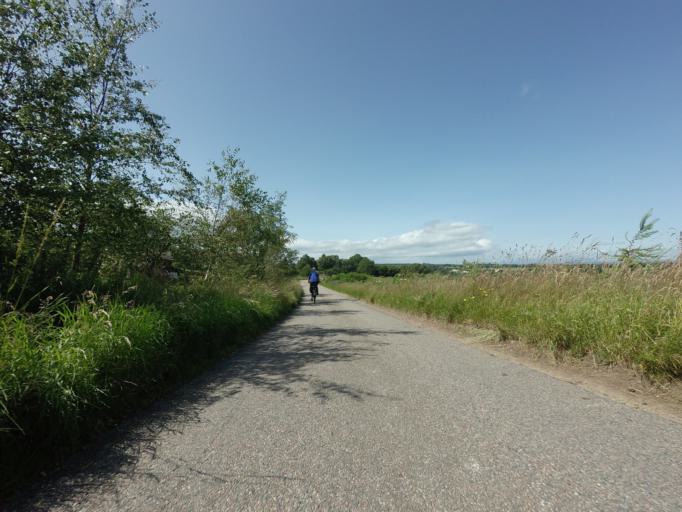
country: GB
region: Scotland
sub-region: Highland
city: Nairn
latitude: 57.5036
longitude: -3.9852
